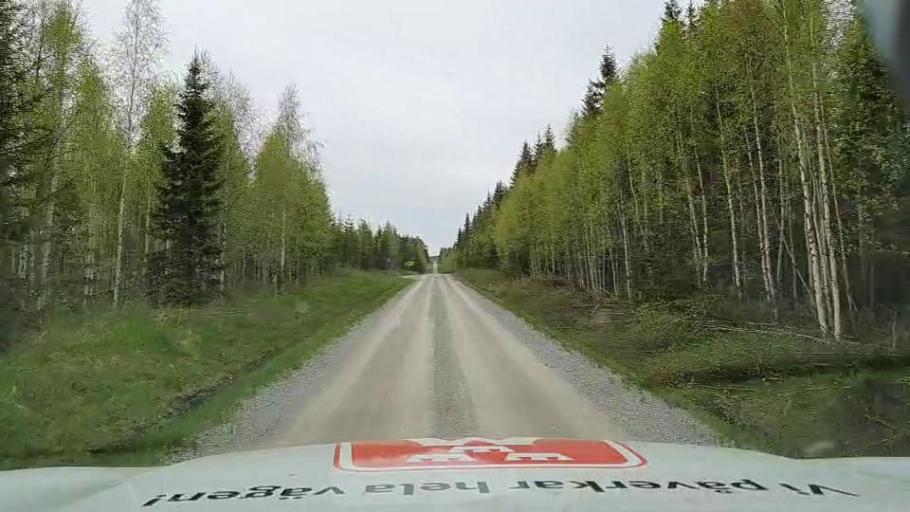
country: SE
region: Jaemtland
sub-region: Bergs Kommun
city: Hoverberg
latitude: 62.8181
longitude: 14.6629
